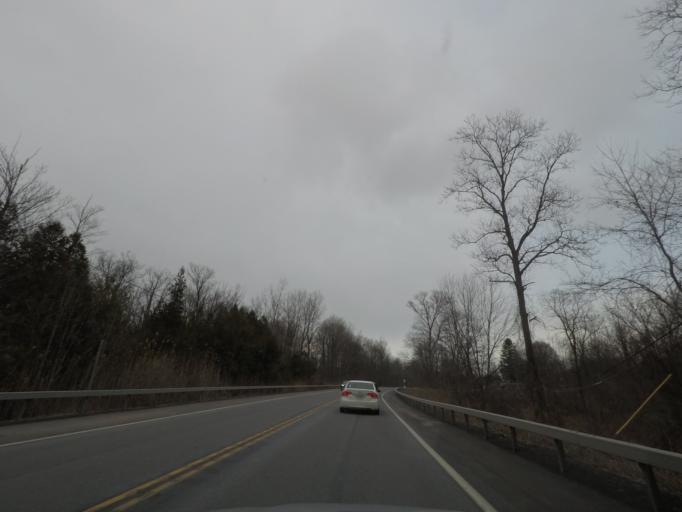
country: US
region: New York
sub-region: Oneida County
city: Sherrill
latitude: 43.0767
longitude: -75.6167
